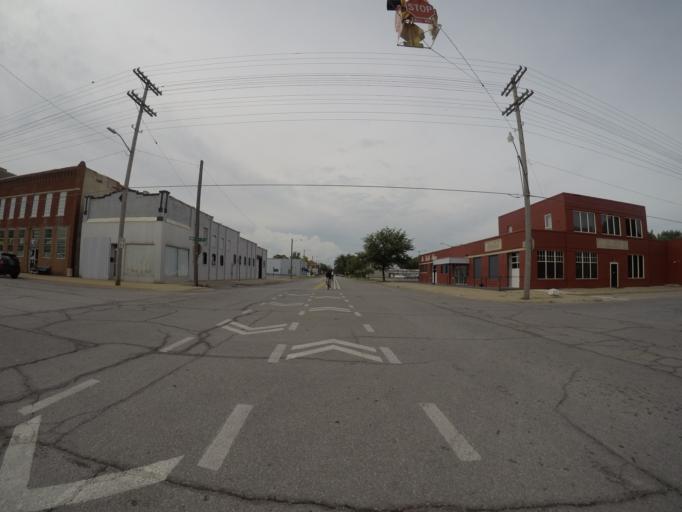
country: US
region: Kansas
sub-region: Franklin County
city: Ottawa
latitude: 38.6158
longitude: -95.2700
